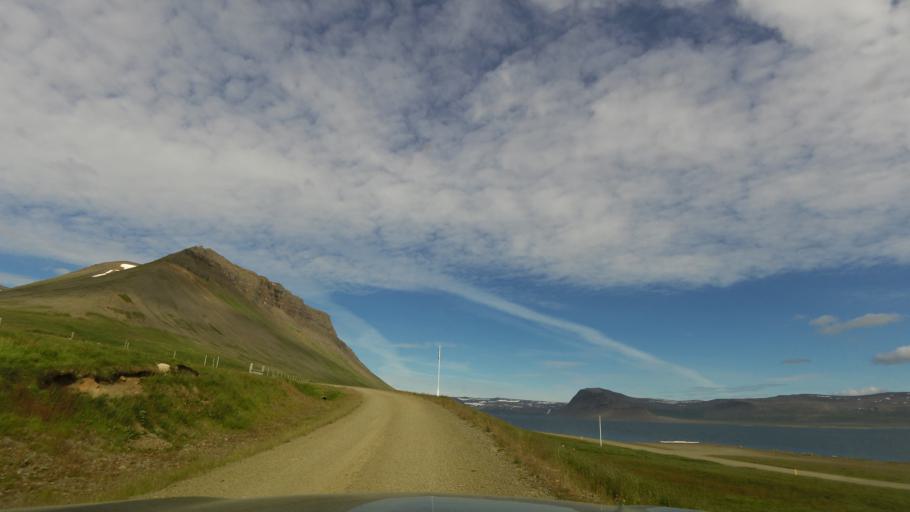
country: IS
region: Westfjords
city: Isafjoerdur
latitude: 65.7577
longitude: -23.4573
